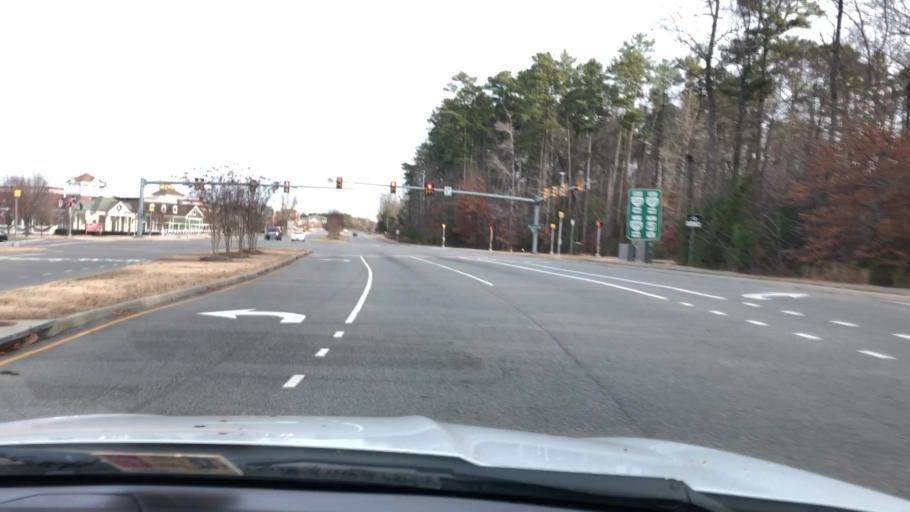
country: US
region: Virginia
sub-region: James City County
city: Williamsburg
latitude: 37.2750
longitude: -76.7387
